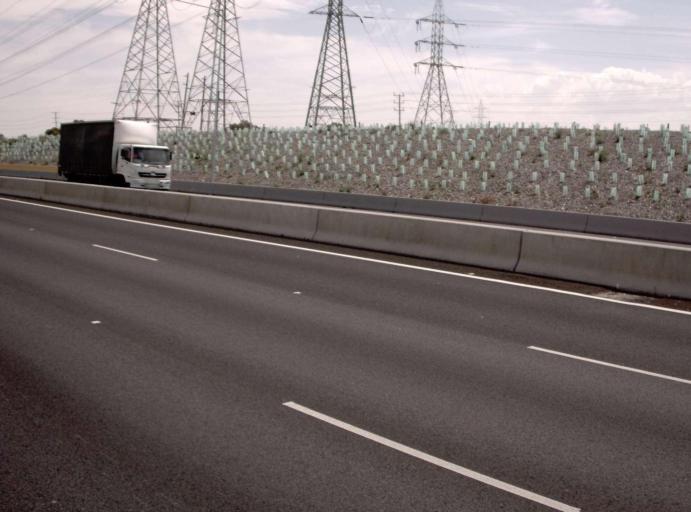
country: AU
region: Victoria
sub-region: Brimbank
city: Albion
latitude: -37.7532
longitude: 144.8287
